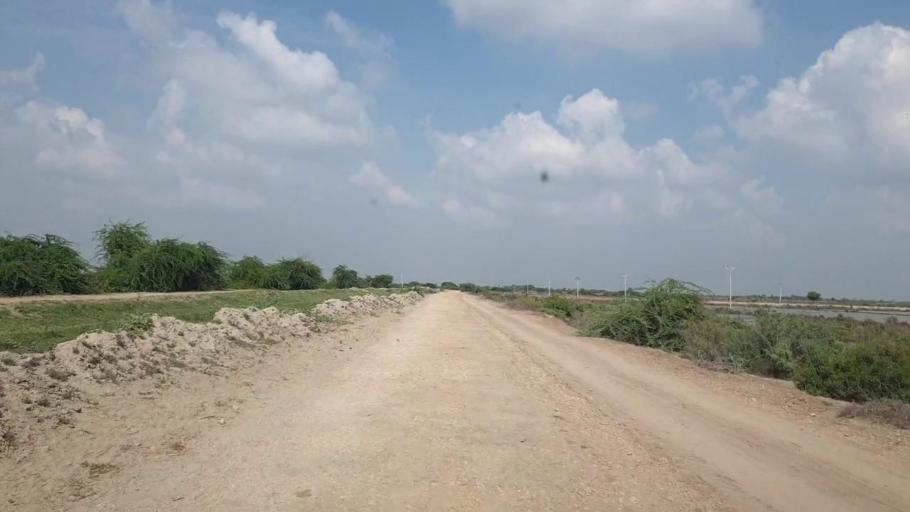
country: PK
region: Sindh
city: Badin
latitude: 24.5045
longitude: 68.6558
